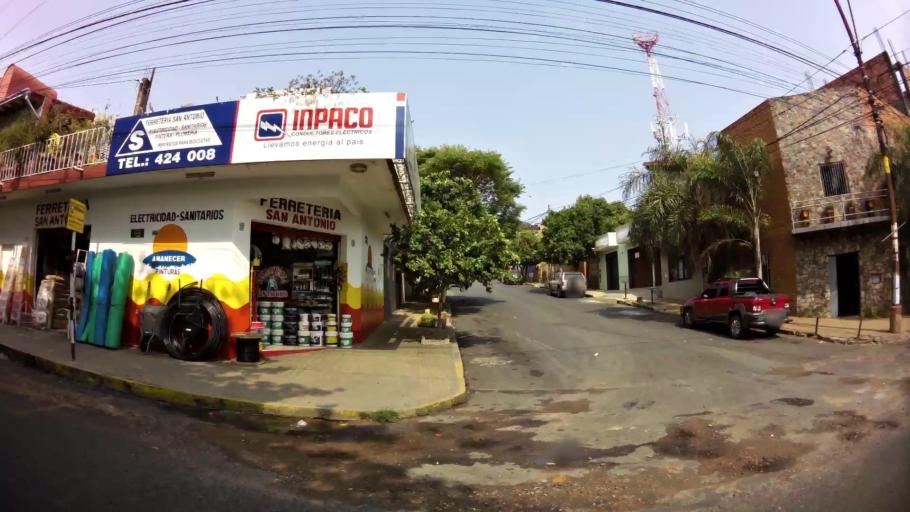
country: PY
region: Presidente Hayes
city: Nanawa
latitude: -25.2853
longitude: -57.6538
